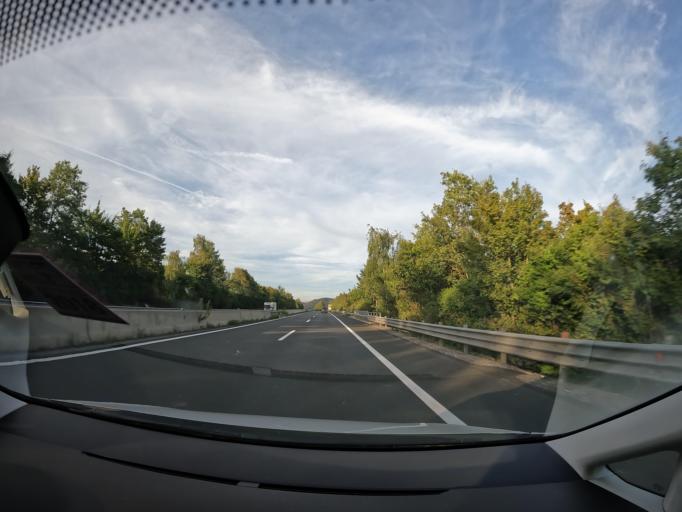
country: AT
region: Carinthia
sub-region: Politischer Bezirk Volkermarkt
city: Griffen
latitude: 46.6904
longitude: 14.7071
